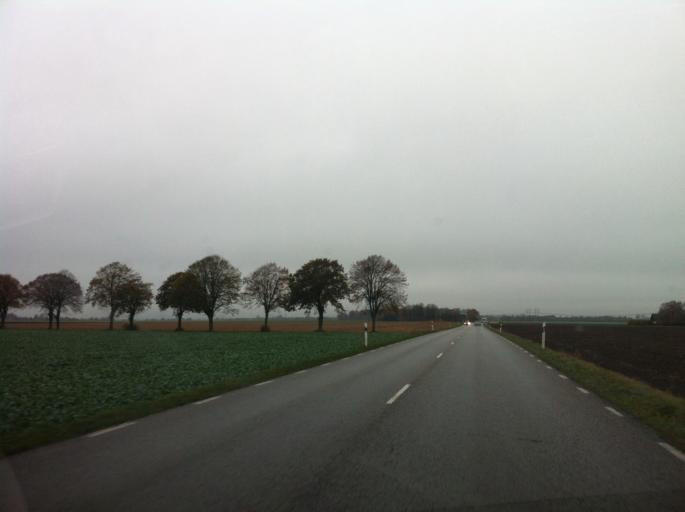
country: SE
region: Skane
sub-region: Kavlinge Kommun
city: Kaevlinge
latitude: 55.8023
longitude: 13.0884
